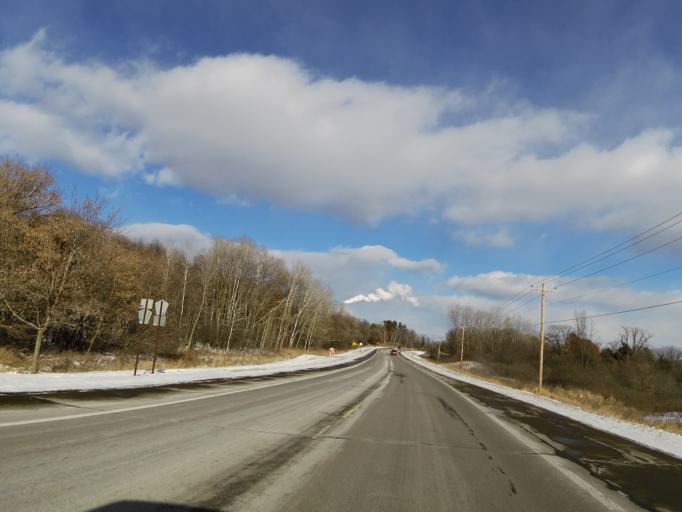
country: US
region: Minnesota
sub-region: Washington County
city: Oak Park Heights
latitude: 45.0164
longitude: -92.8052
